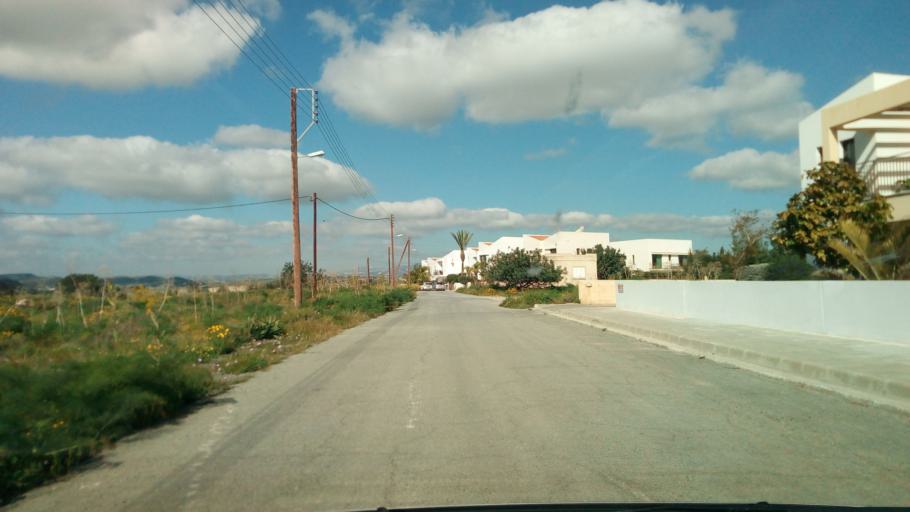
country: CY
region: Larnaka
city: Tersefanou
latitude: 34.8090
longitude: 33.4864
